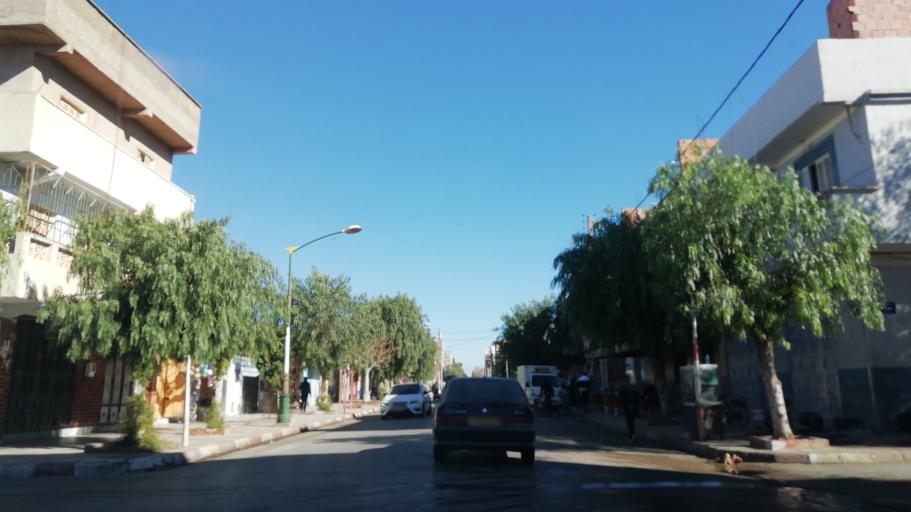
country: DZ
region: Tlemcen
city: Beni Mester
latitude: 34.8282
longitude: -1.5283
